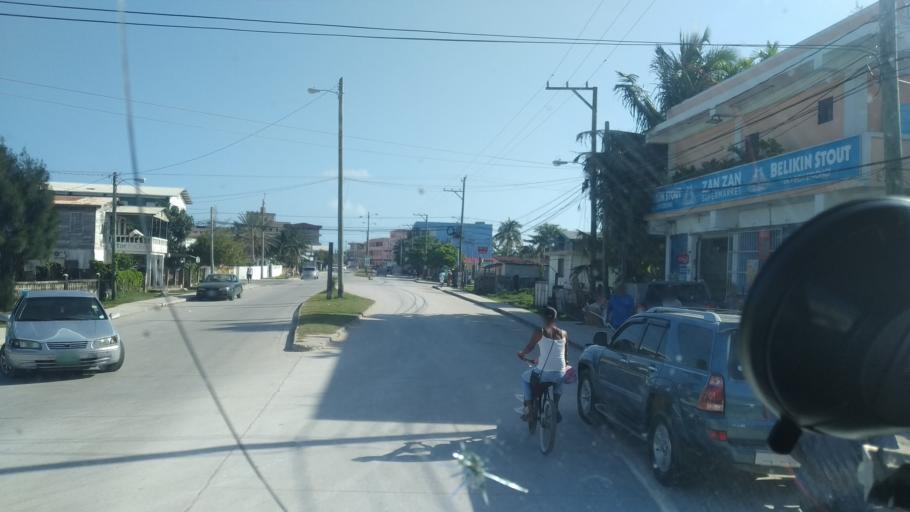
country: BZ
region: Belize
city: Belize City
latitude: 17.4879
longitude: -88.2009
